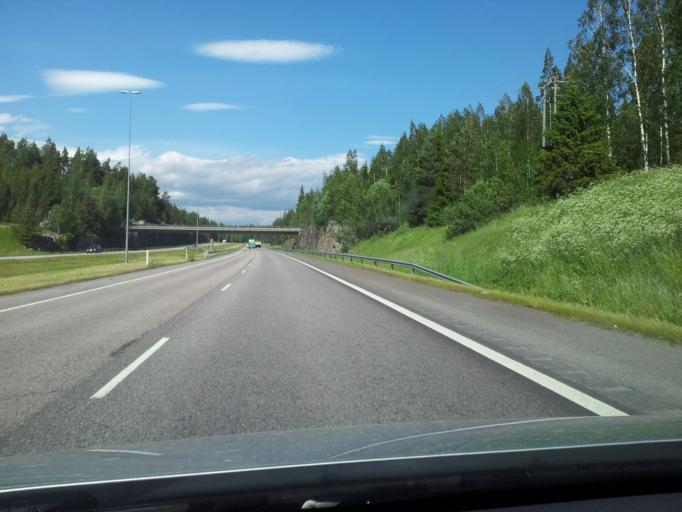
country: FI
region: Uusimaa
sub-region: Porvoo
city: Porvoo
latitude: 60.3453
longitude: 25.5133
